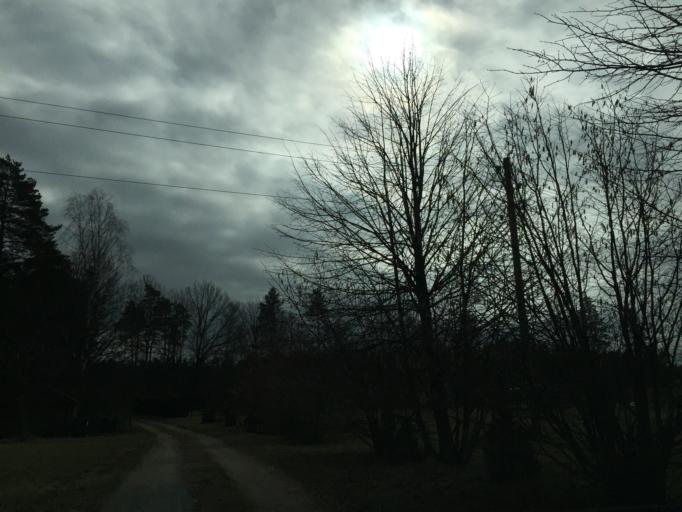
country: LV
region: Garkalne
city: Garkalne
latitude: 57.0746
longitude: 24.4283
